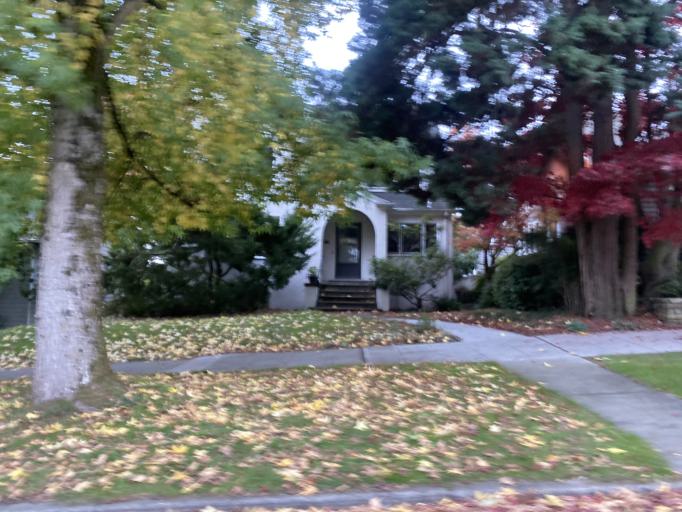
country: US
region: Washington
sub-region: King County
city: Seattle
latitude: 47.6464
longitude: -122.3033
